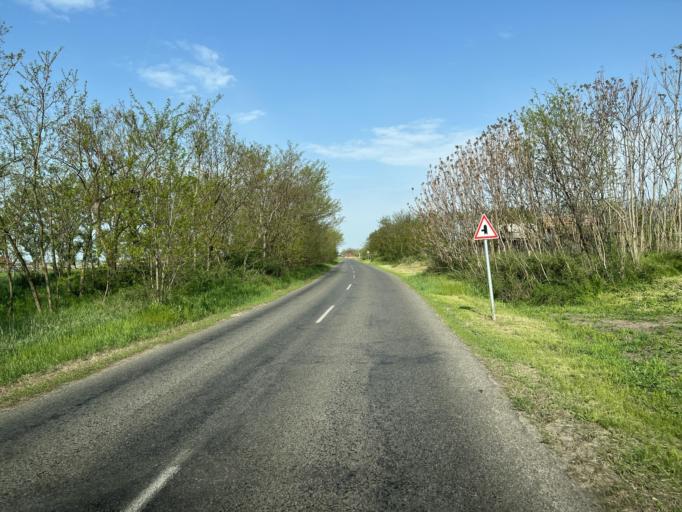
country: HU
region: Pest
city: Jaszkarajeno
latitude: 47.0421
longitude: 20.1005
